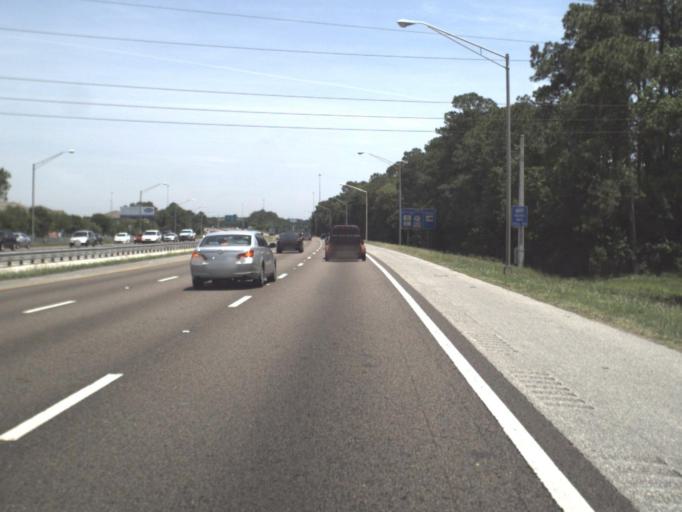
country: US
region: Florida
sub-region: Saint Johns County
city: Fruit Cove
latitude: 30.1716
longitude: -81.6123
